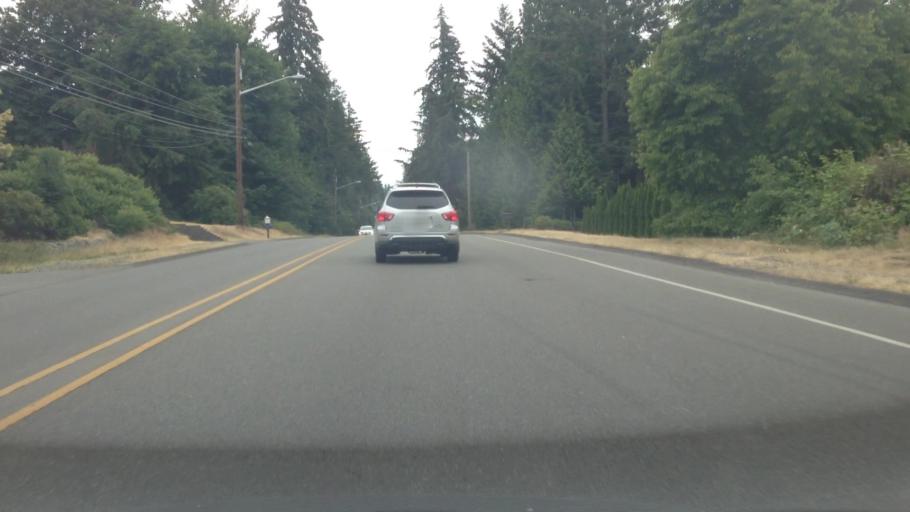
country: US
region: Washington
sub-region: Pierce County
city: South Hill
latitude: 47.1319
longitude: -122.3040
